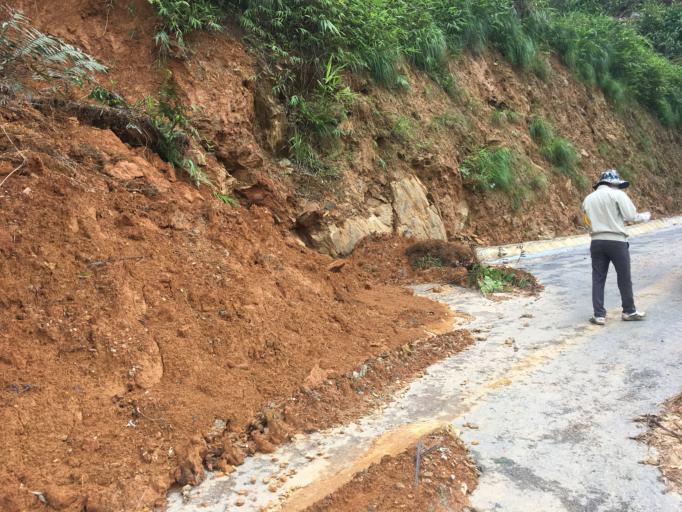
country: VN
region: Ha Giang
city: Thi Tran Tam Son
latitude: 22.9821
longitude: 105.0581
